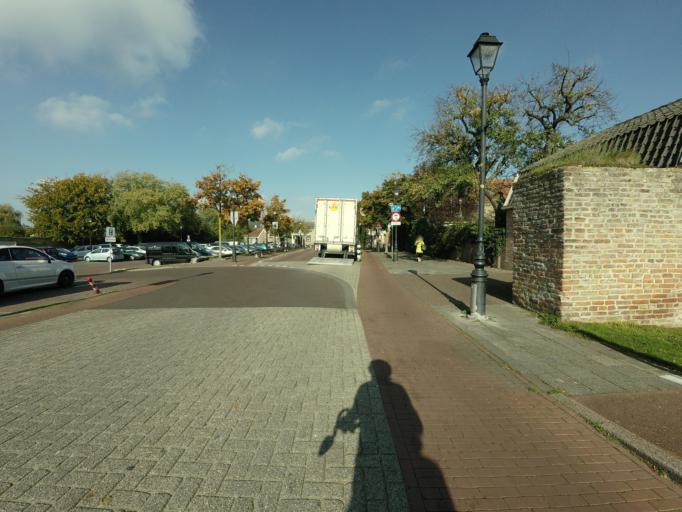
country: NL
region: Gelderland
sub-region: Gemeente Culemborg
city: Culemborg
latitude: 51.9559
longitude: 5.2245
